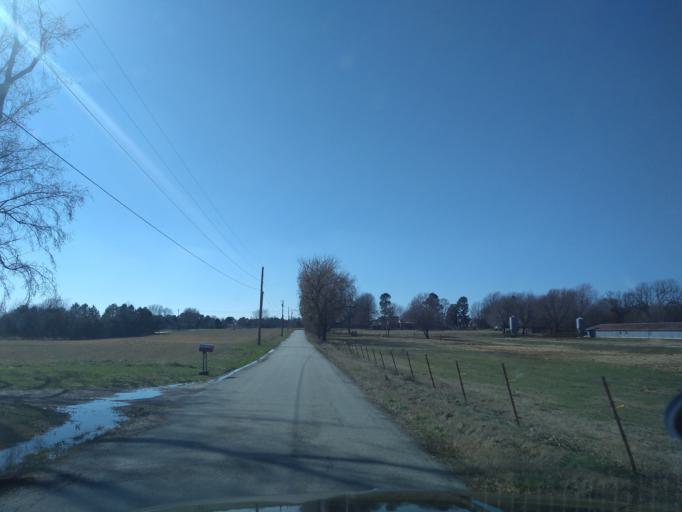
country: US
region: Arkansas
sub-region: Washington County
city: Farmington
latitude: 36.0675
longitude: -94.2501
